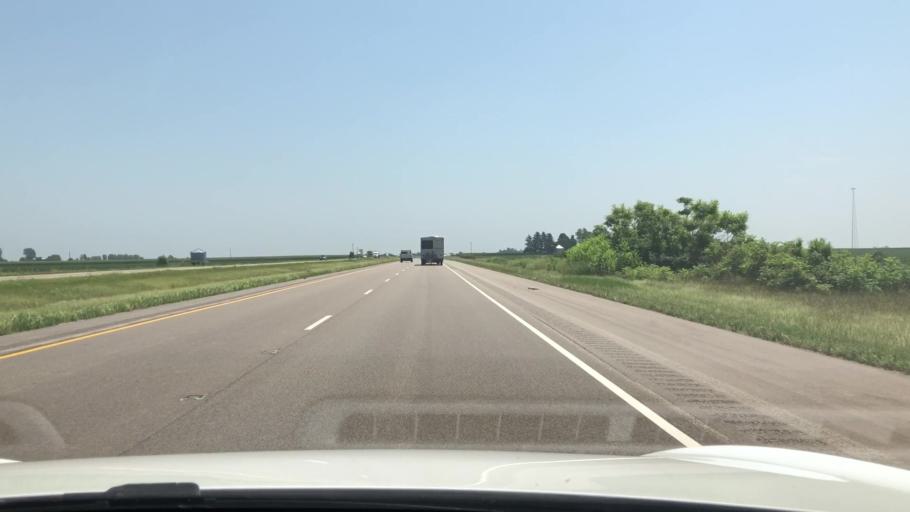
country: US
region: Illinois
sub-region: De Witt County
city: Farmer City
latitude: 40.2938
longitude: -88.7037
